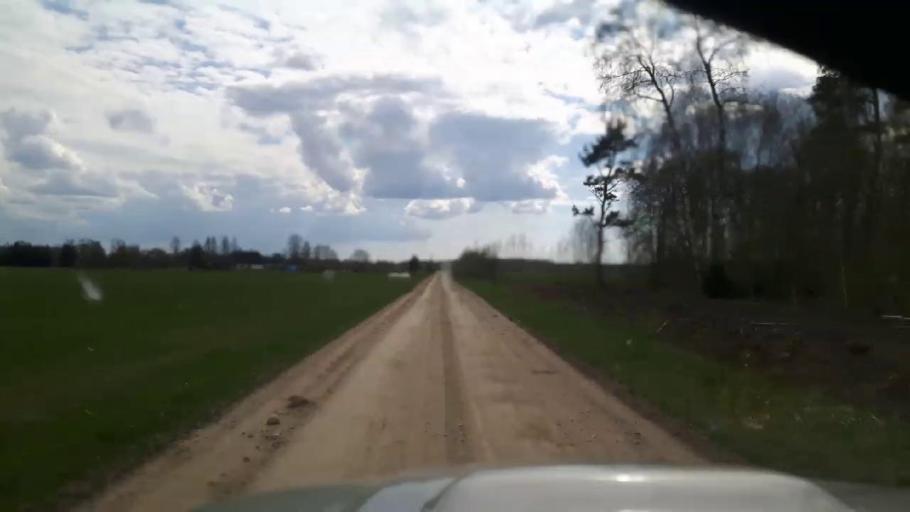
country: EE
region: Paernumaa
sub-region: Tootsi vald
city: Tootsi
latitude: 58.5135
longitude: 24.8465
